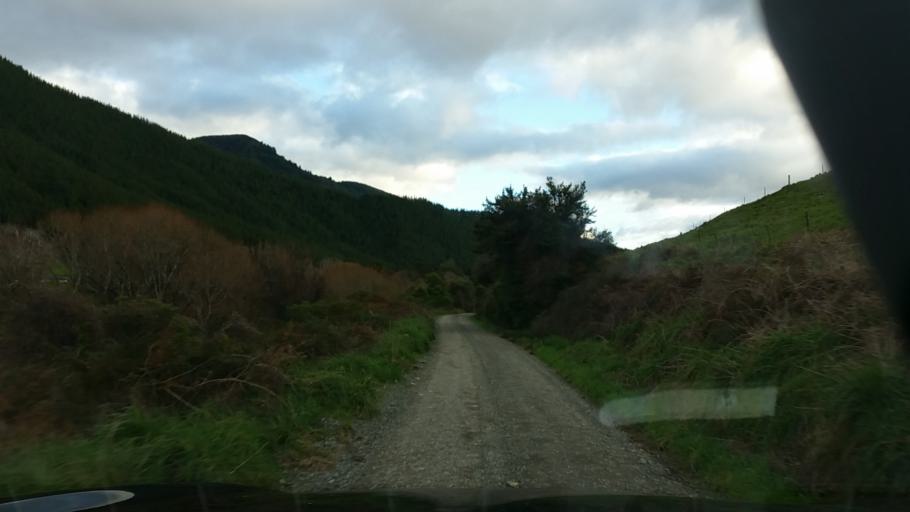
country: NZ
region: Nelson
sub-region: Nelson City
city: Nelson
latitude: -41.2091
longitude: 173.6331
